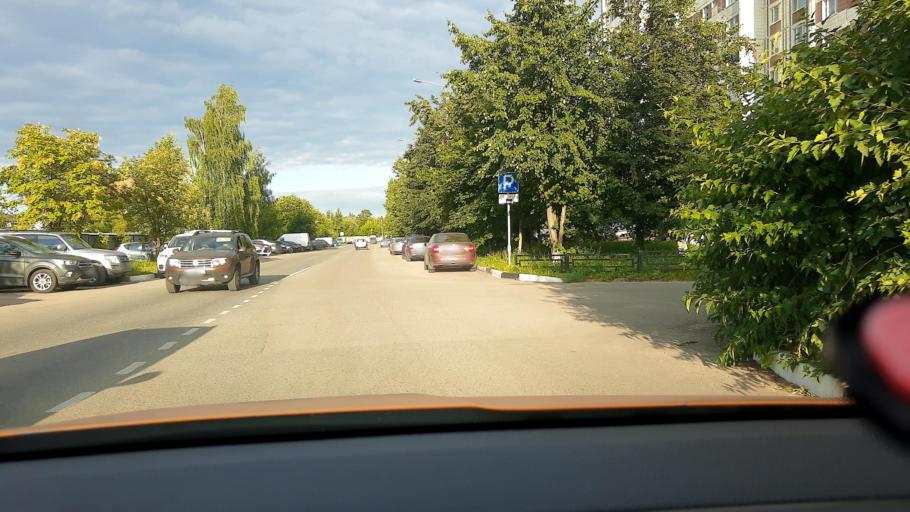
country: RU
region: Moskovskaya
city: Krasnoznamensk
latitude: 55.6042
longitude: 37.0322
